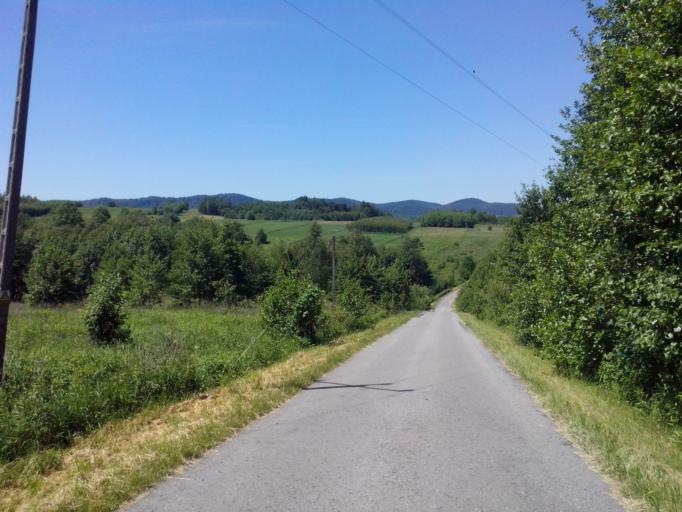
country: PL
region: Subcarpathian Voivodeship
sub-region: Powiat strzyzowski
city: Wysoka Strzyzowska
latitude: 49.8190
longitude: 21.7623
